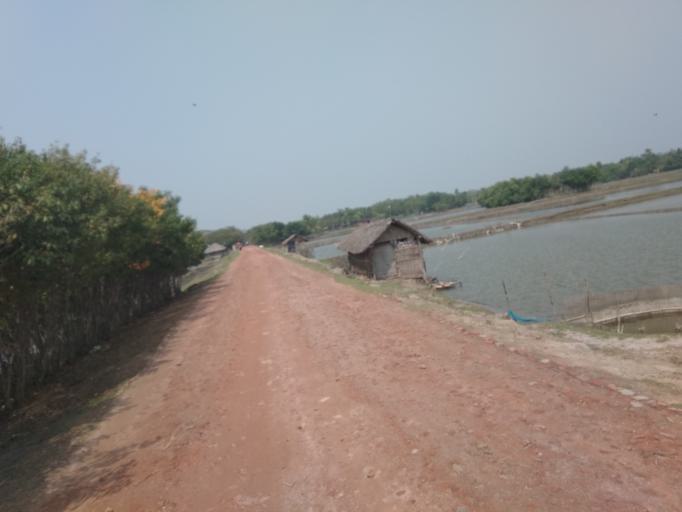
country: IN
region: West Bengal
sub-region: North 24 Parganas
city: Taki
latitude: 22.2963
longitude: 89.2702
